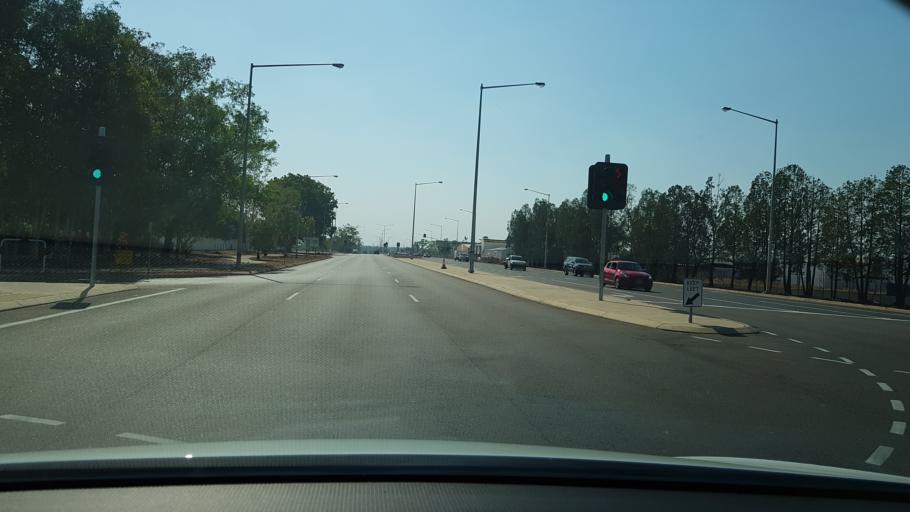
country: AU
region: Northern Territory
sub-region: Palmerston
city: Palmerston
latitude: -12.4777
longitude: 130.9869
